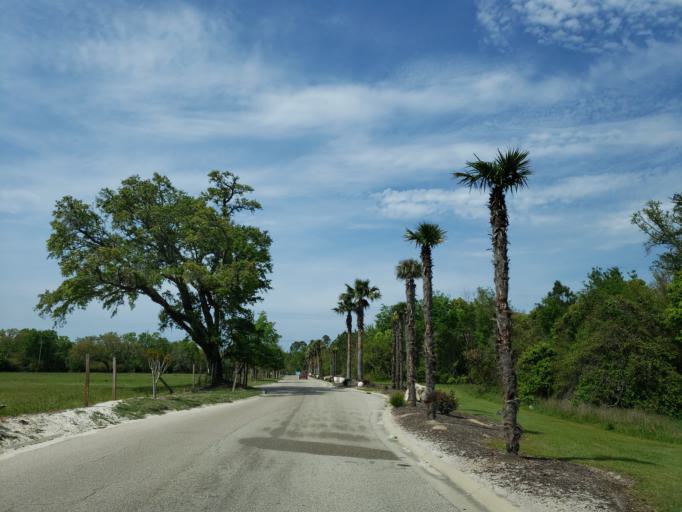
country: US
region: Mississippi
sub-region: Harrison County
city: Biloxi
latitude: 30.3907
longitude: -88.9835
